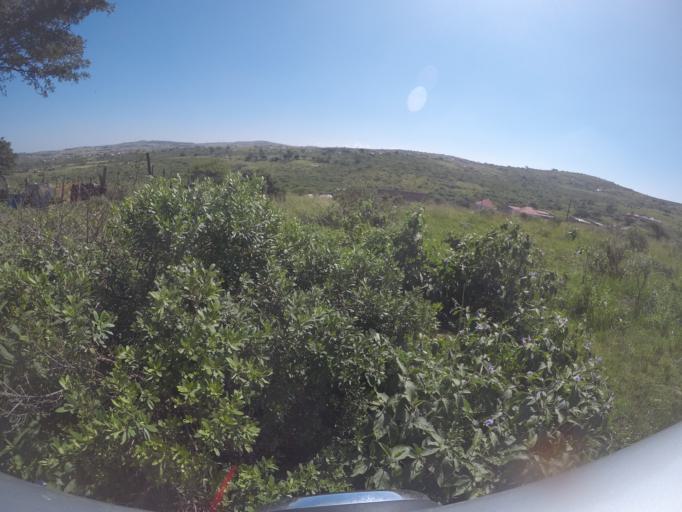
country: ZA
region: KwaZulu-Natal
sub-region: uThungulu District Municipality
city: Empangeni
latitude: -28.5699
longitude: 31.6988
